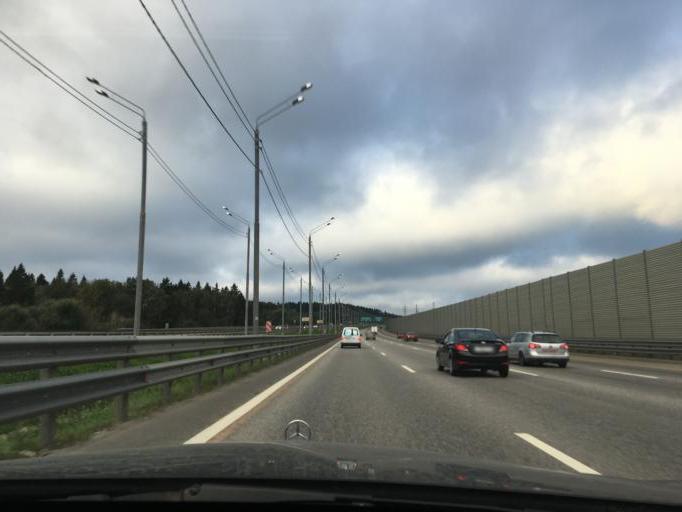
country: RU
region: Moskovskaya
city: Pavlovskaya Sloboda
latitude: 55.7869
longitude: 37.1149
